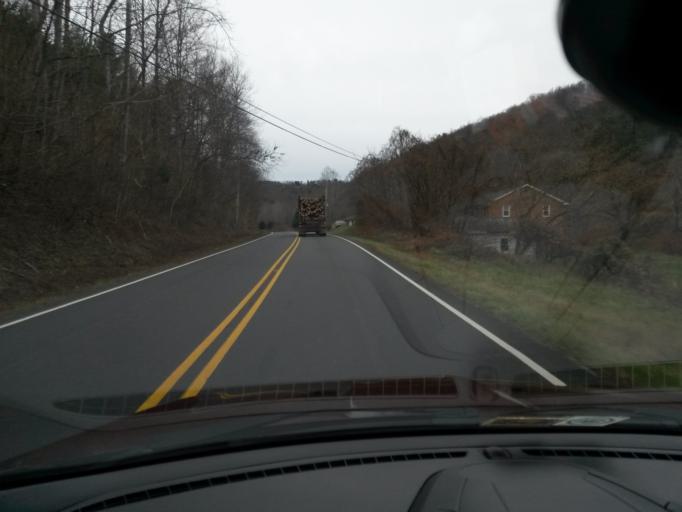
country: US
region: Virginia
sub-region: City of Buena Vista
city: Buena Vista
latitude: 37.6825
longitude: -79.2247
